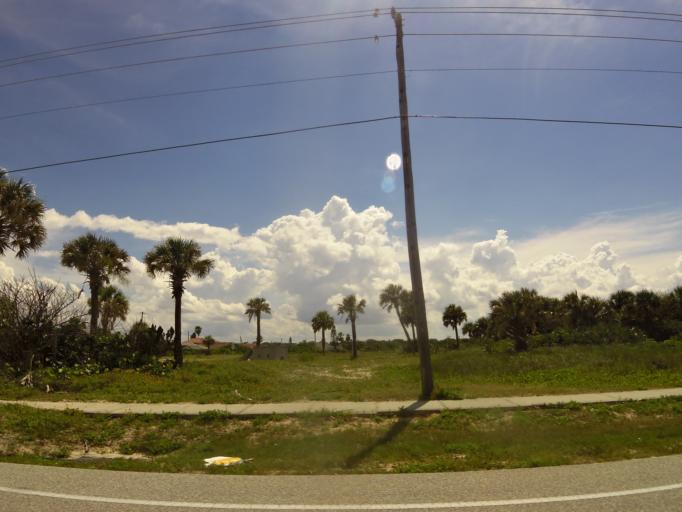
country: US
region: Florida
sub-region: Volusia County
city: Ormond-by-the-Sea
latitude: 29.3471
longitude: -81.0654
